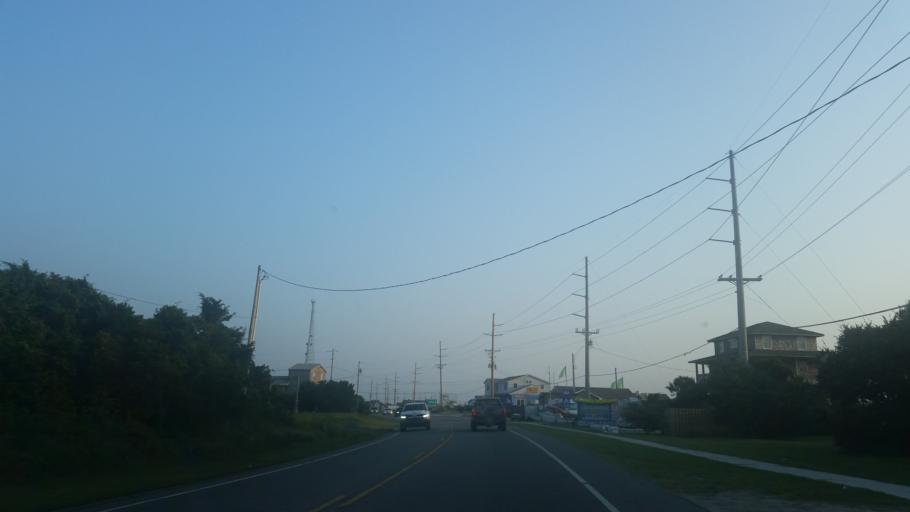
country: US
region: North Carolina
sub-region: Dare County
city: Wanchese
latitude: 35.5896
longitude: -75.4683
